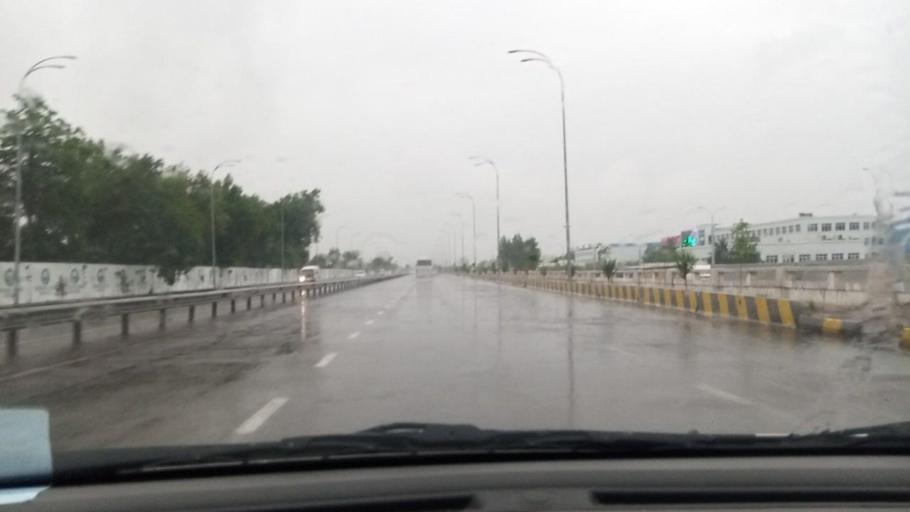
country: UZ
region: Toshkent Shahri
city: Bektemir
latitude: 41.2660
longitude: 69.3688
